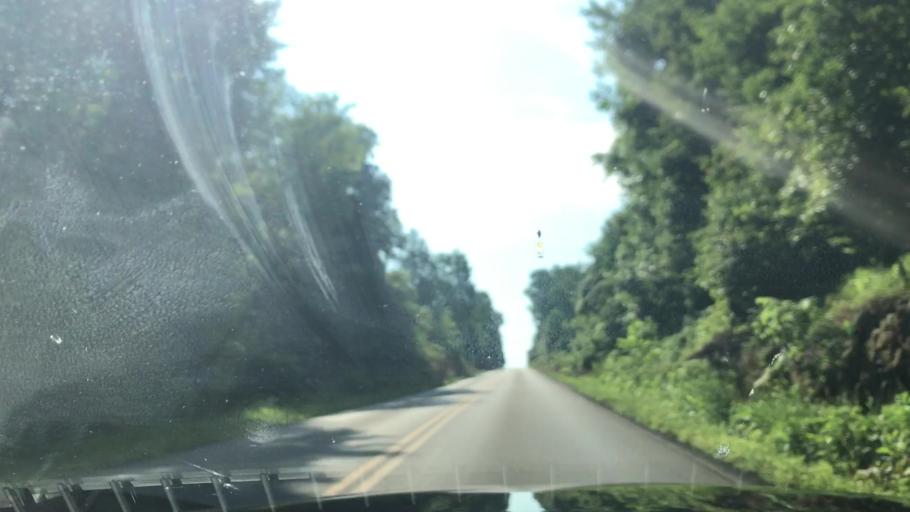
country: US
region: Kentucky
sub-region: Green County
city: Greensburg
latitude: 37.2269
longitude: -85.6710
